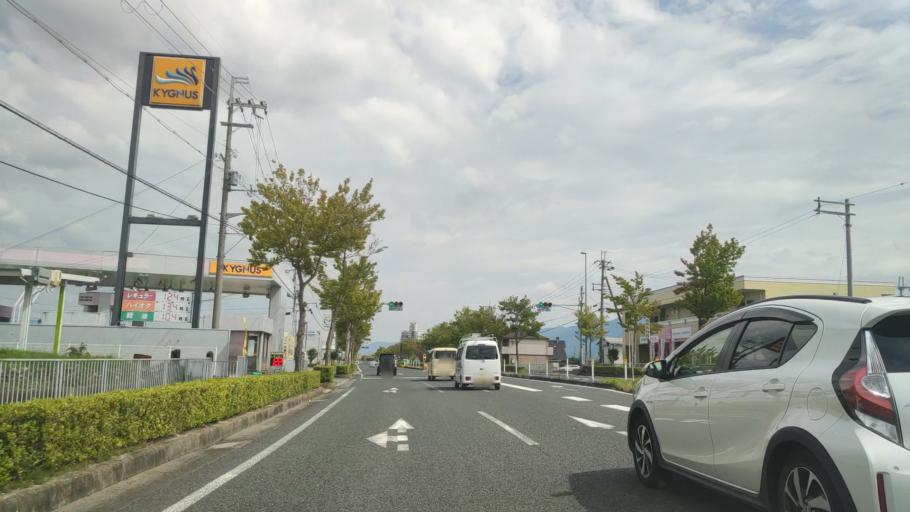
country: JP
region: Wakayama
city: Iwade
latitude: 34.2599
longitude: 135.3429
